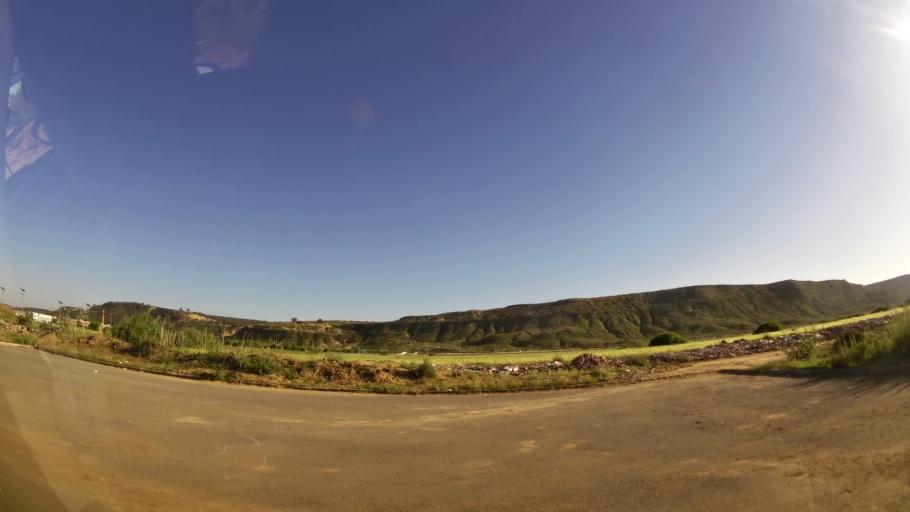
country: MA
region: Oriental
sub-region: Berkane-Taourirt
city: Madagh
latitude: 35.0767
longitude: -2.2466
